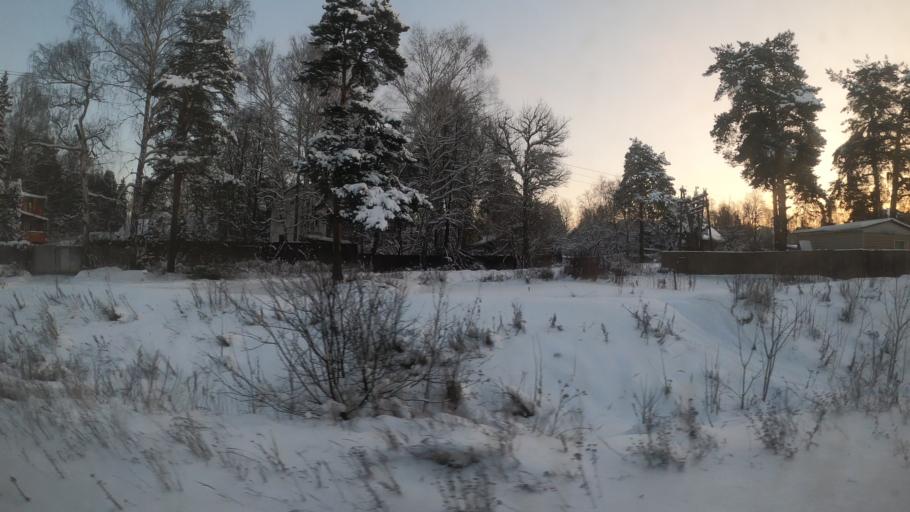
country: RU
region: Moskovskaya
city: Dedenevo
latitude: 56.2461
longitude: 37.5111
